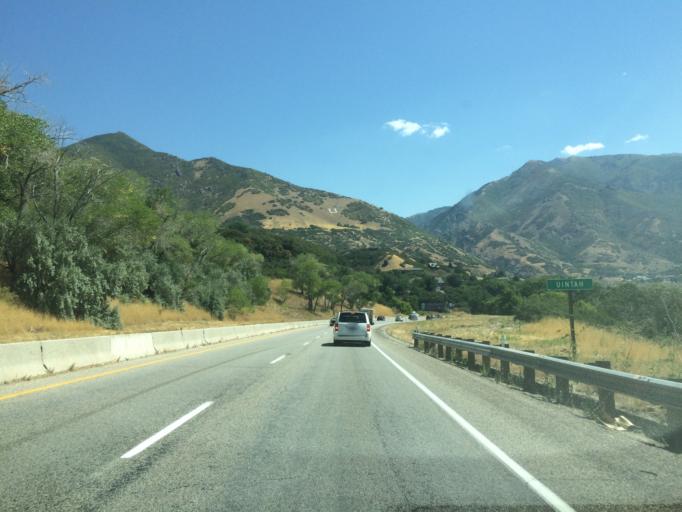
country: US
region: Utah
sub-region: Weber County
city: Uintah
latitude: 41.1471
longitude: -111.9236
